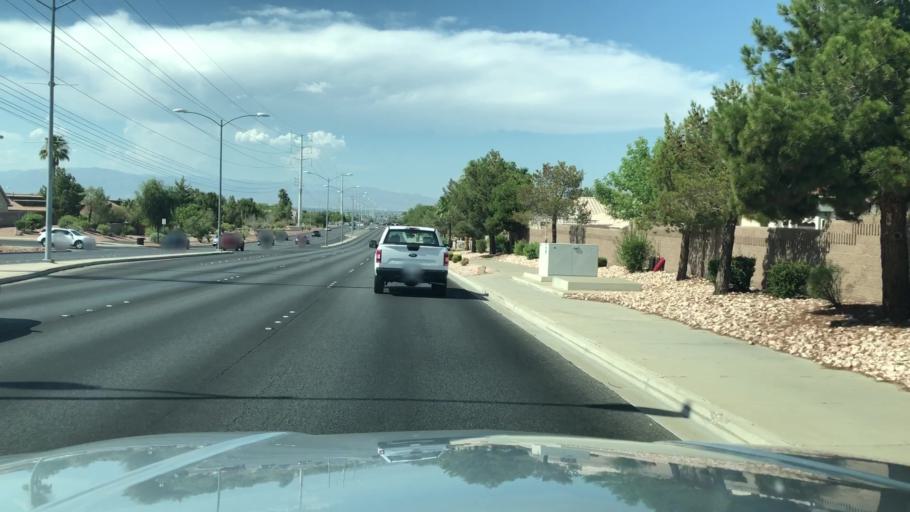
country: US
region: Nevada
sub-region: Clark County
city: Whitney
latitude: 36.0499
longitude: -115.0463
